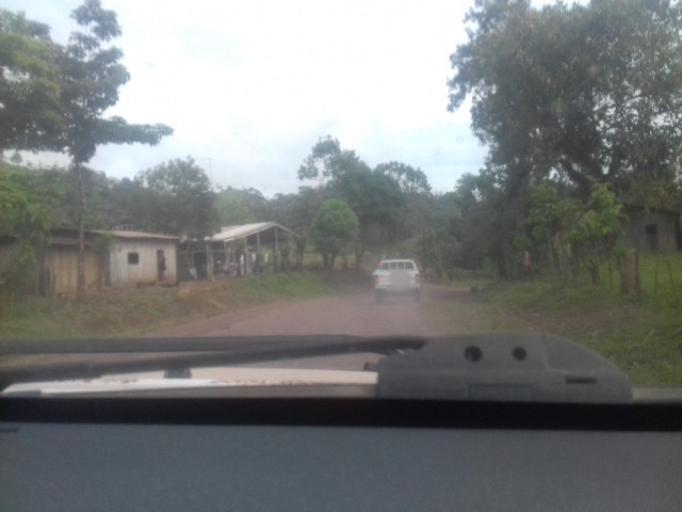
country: NI
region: Atlantico Norte (RAAN)
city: Waslala
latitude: 13.4123
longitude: -85.3201
